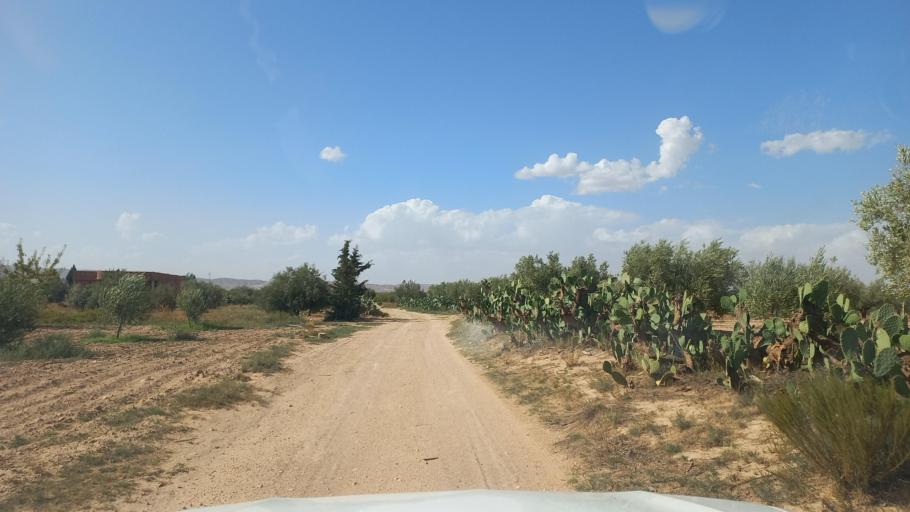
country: TN
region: Al Qasrayn
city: Sbiba
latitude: 35.3006
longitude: 9.0422
